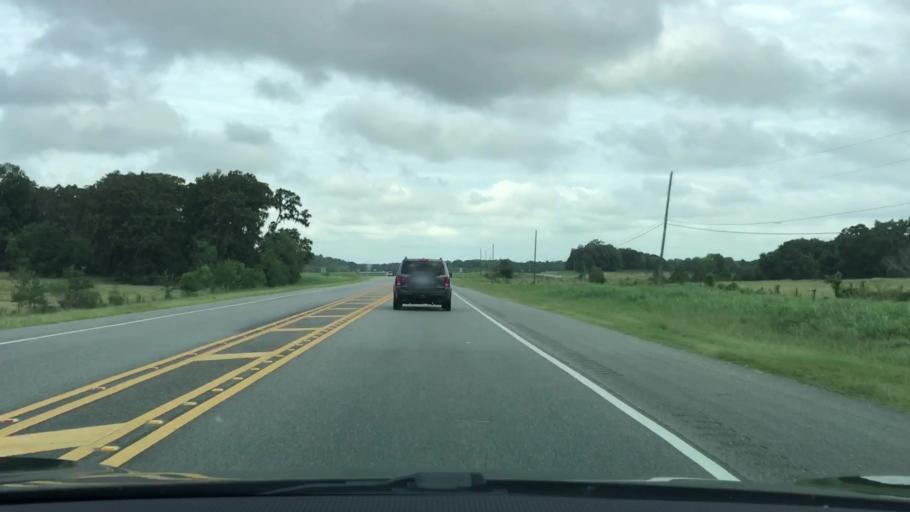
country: US
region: Alabama
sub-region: Montgomery County
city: Pike Road
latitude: 32.3320
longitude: -86.0566
